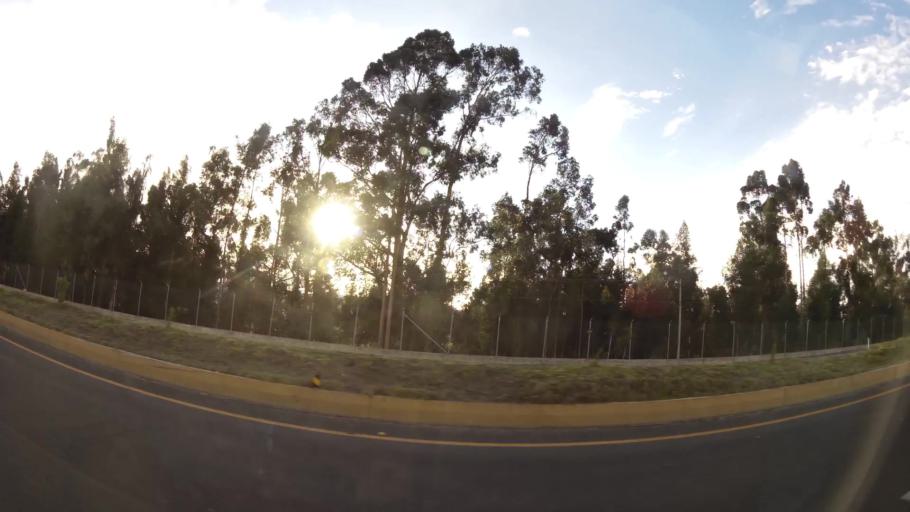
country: EC
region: Cotopaxi
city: Saquisili
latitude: -0.8471
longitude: -78.6194
